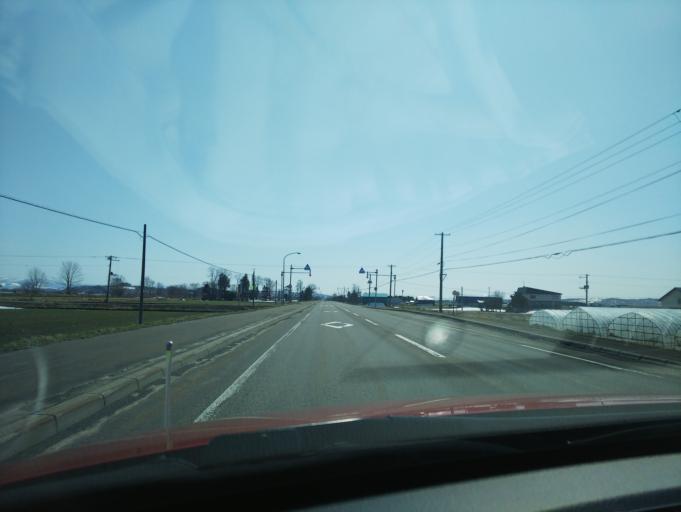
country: JP
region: Hokkaido
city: Nayoro
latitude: 44.2065
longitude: 142.3949
